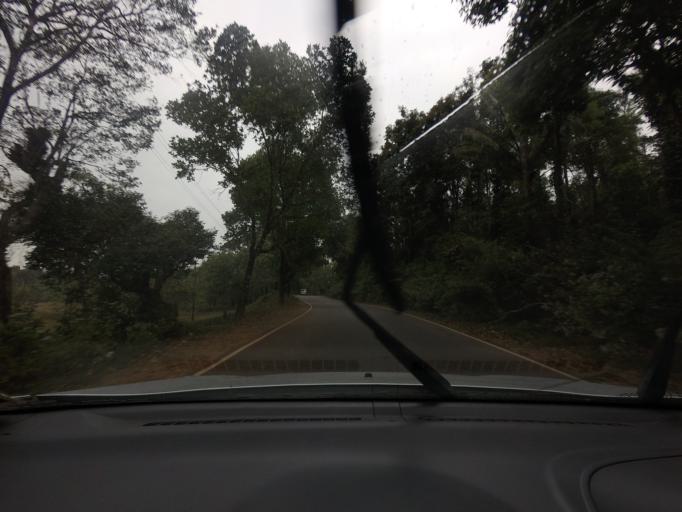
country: IN
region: Karnataka
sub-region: Hassan
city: Sakleshpur
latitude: 12.9819
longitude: 75.7190
